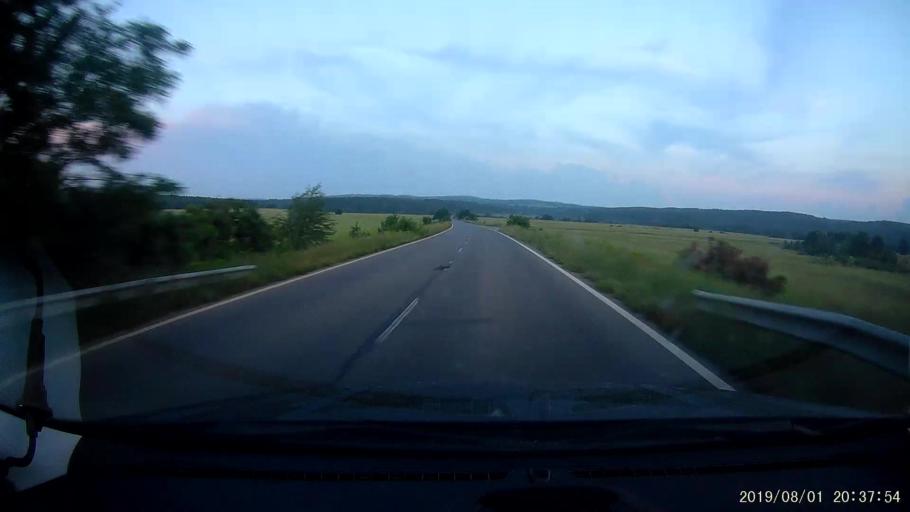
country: BG
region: Yambol
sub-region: Obshtina Elkhovo
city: Elkhovo
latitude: 42.0380
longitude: 26.5964
